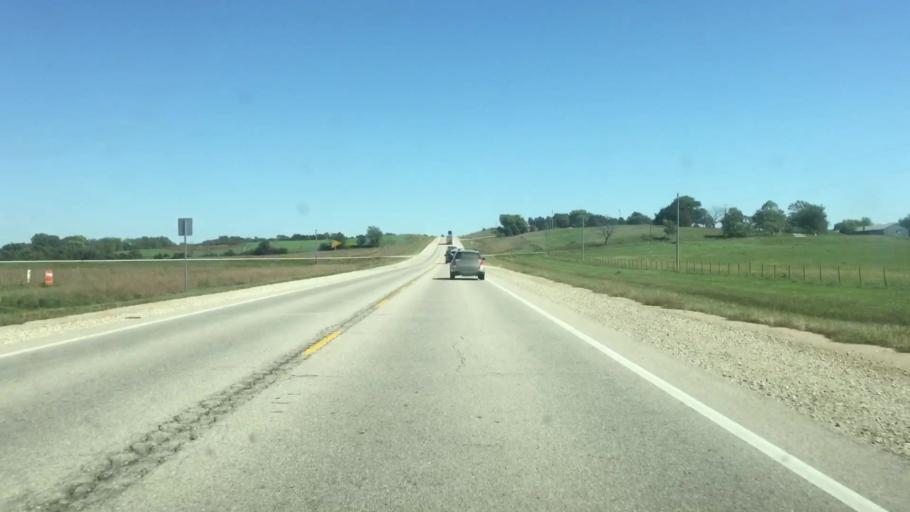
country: US
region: Kansas
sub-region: Nemaha County
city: Seneca
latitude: 39.8424
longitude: -95.9994
